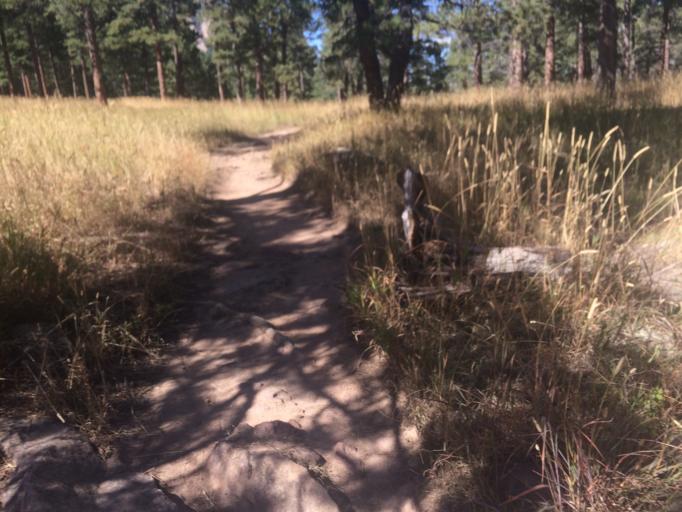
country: US
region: Colorado
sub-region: Boulder County
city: Boulder
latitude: 39.9677
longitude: -105.2815
